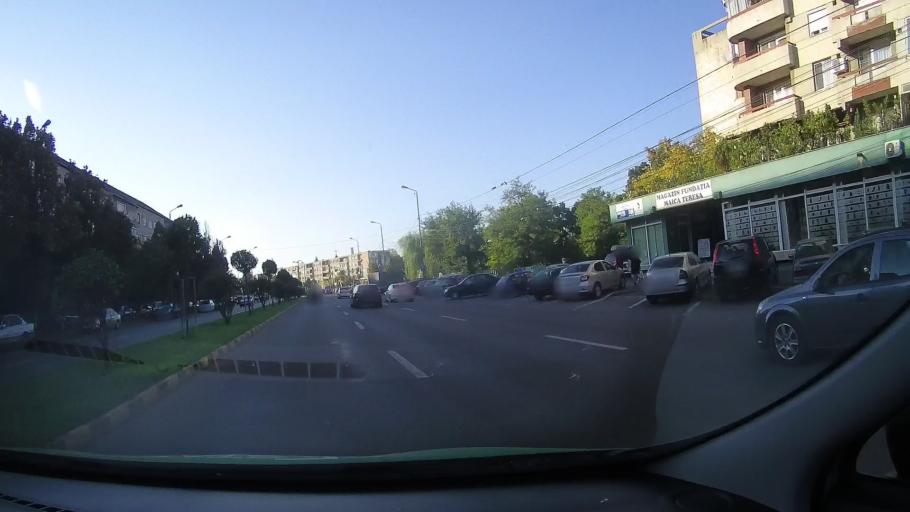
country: RO
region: Bihor
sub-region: Comuna Biharea
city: Oradea
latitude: 47.0727
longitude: 21.9165
